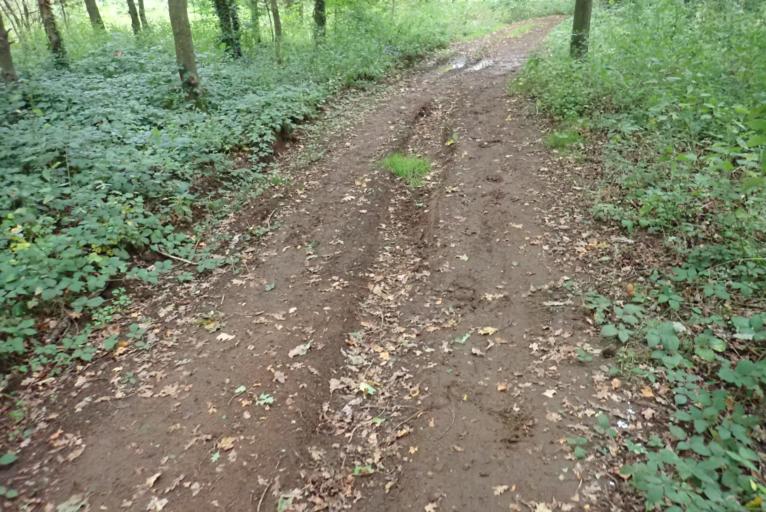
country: BE
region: Flanders
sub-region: Provincie Antwerpen
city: Hulshout
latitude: 51.0641
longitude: 4.8134
